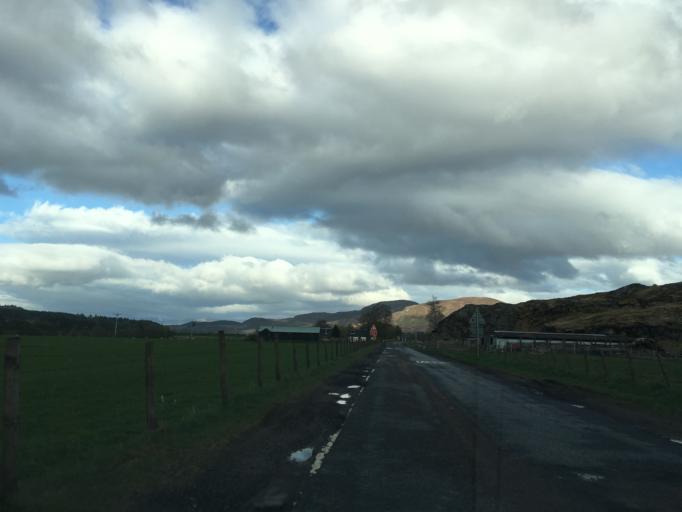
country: GB
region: Scotland
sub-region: Highland
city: Kingussie
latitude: 57.0138
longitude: -4.2780
